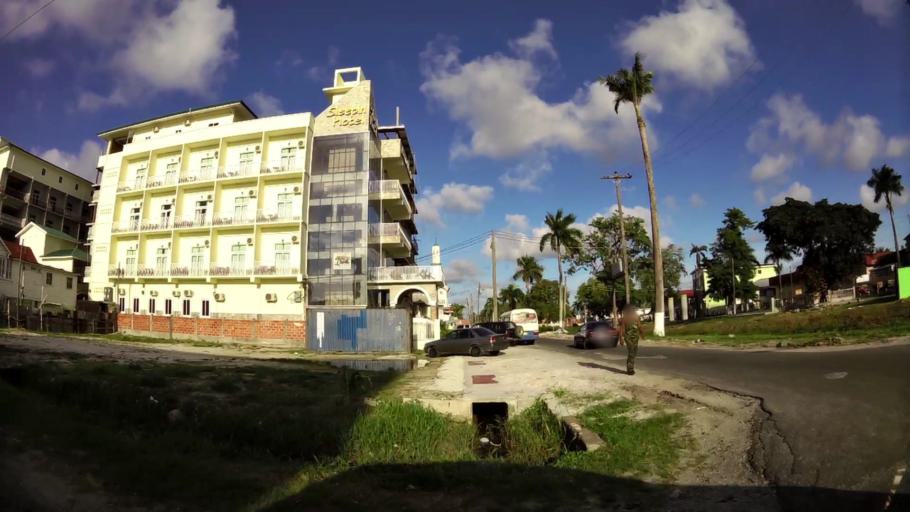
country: GY
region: Demerara-Mahaica
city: Georgetown
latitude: 6.8103
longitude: -58.1531
